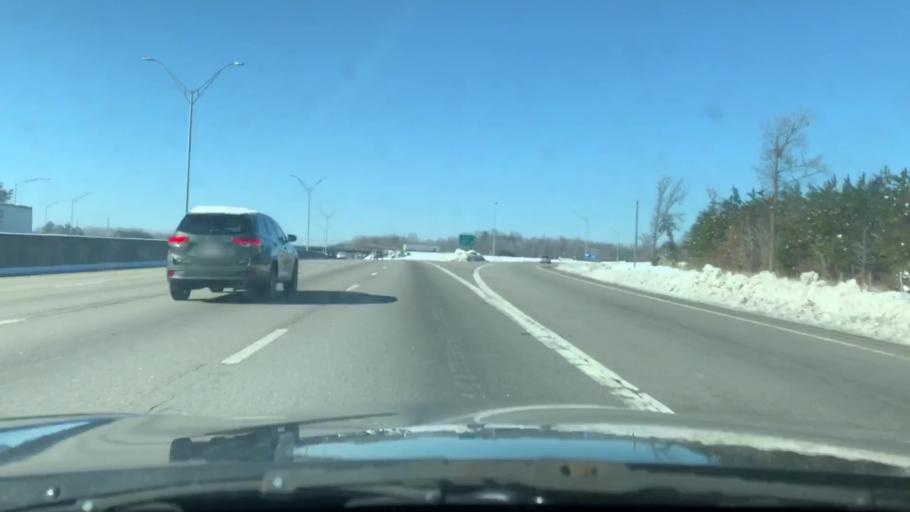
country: US
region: North Carolina
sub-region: Alamance County
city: Mebane
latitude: 36.0792
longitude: -79.2204
